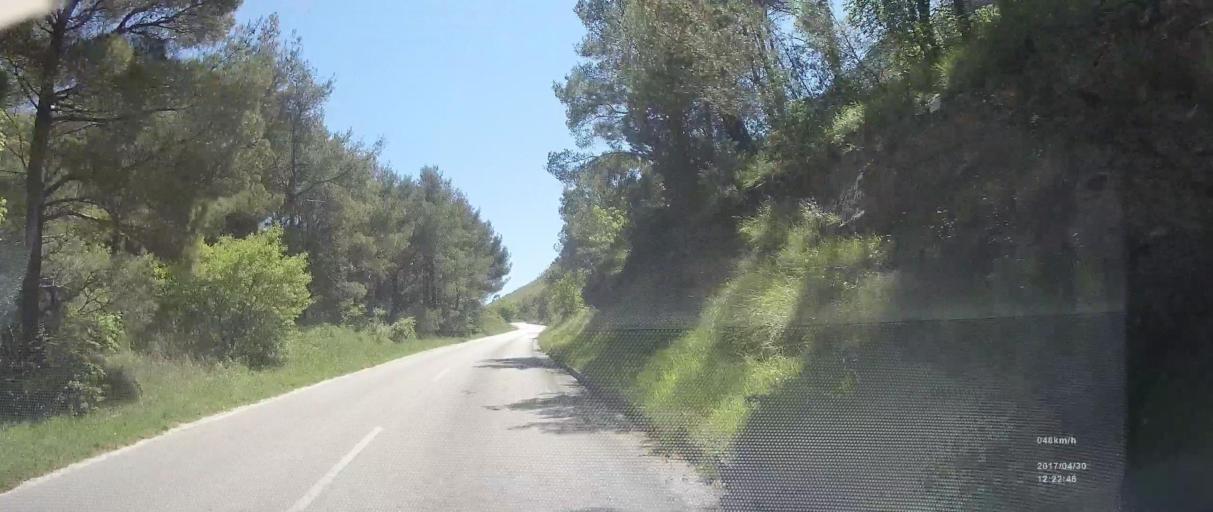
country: HR
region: Splitsko-Dalmatinska
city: Zrnovnica
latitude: 43.5193
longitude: 16.5733
